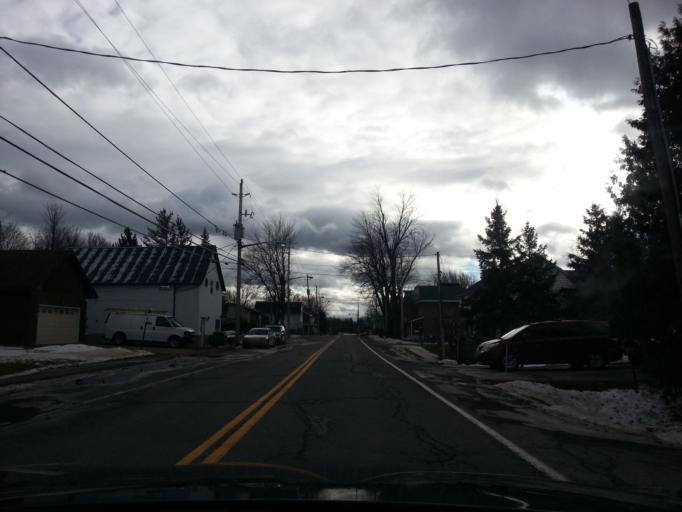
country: CA
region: Ontario
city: Bells Corners
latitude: 45.1511
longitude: -75.6477
